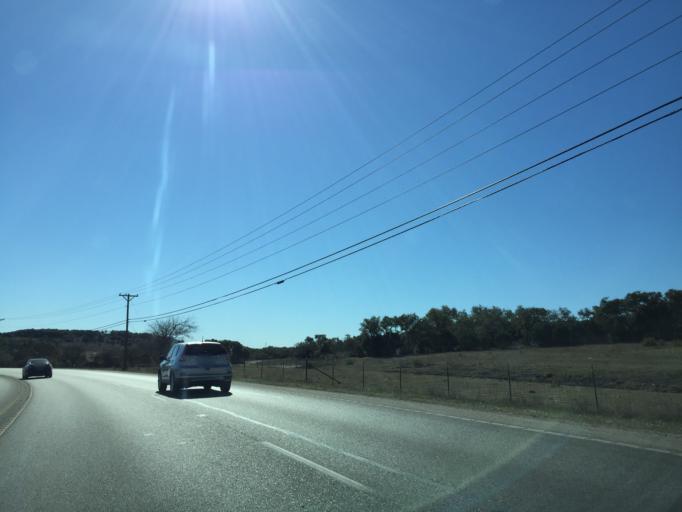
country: US
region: Texas
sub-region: Comal County
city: Canyon Lake
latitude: 29.7871
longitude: -98.3302
